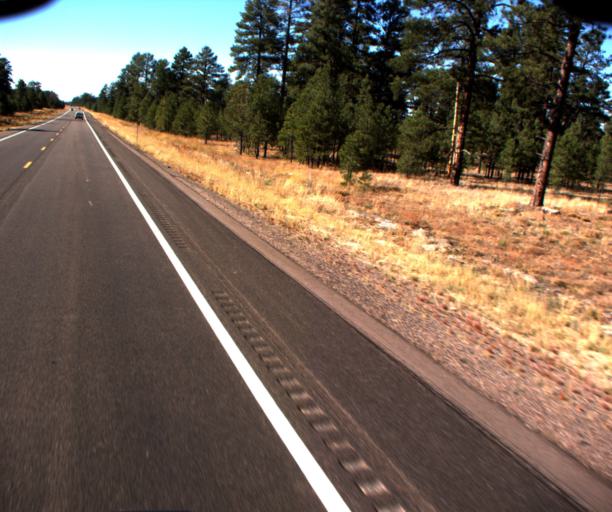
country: US
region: Arizona
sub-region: Apache County
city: Saint Michaels
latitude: 35.6950
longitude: -109.2708
